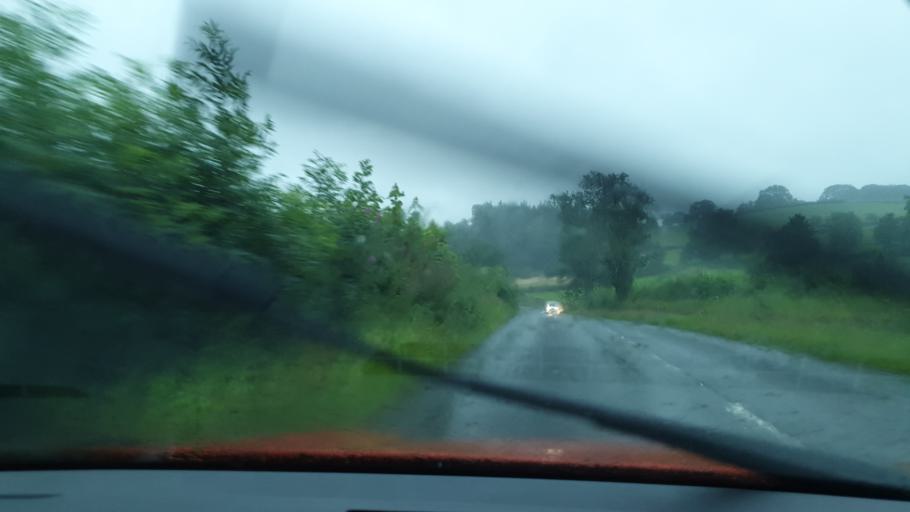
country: GB
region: England
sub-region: Cumbria
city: Ulverston
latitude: 54.2445
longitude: -3.0651
